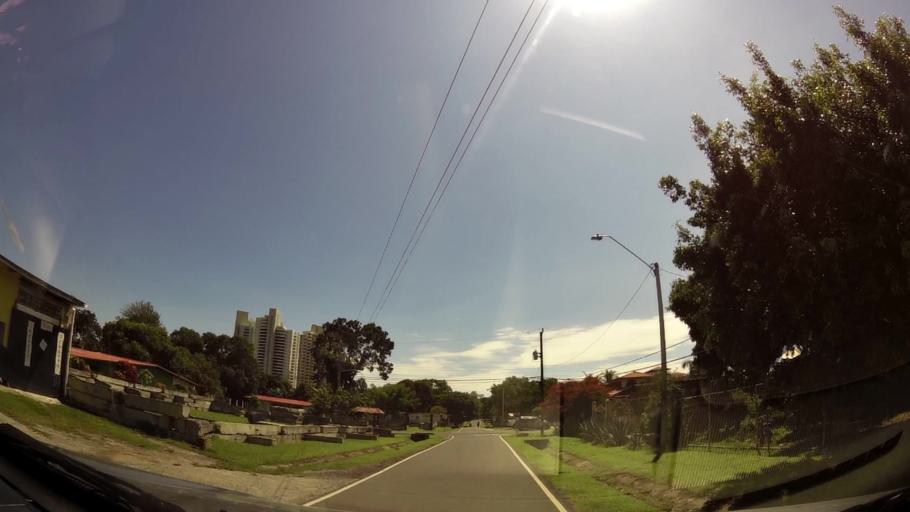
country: PA
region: Panama
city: Nueva Gorgona
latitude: 8.5517
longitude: -79.8731
